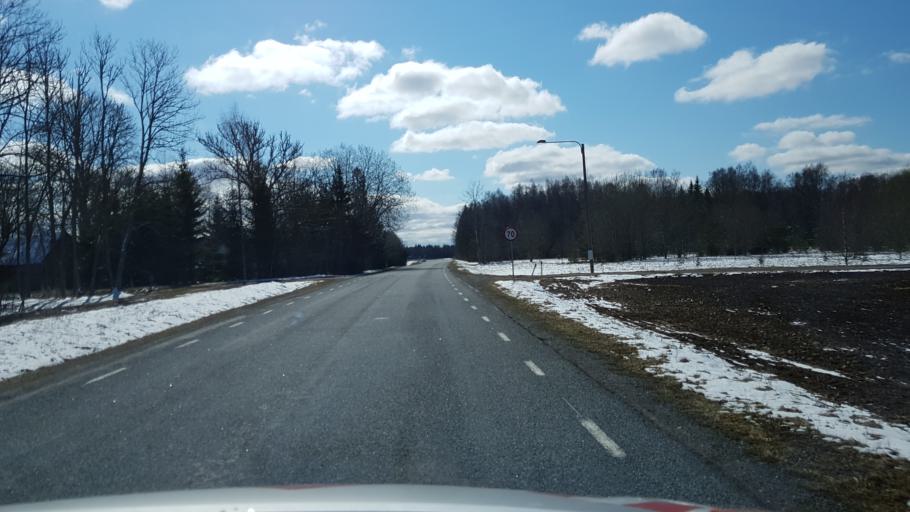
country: EE
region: Laeaene-Virumaa
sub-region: Kadrina vald
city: Kadrina
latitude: 59.4711
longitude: 25.9981
